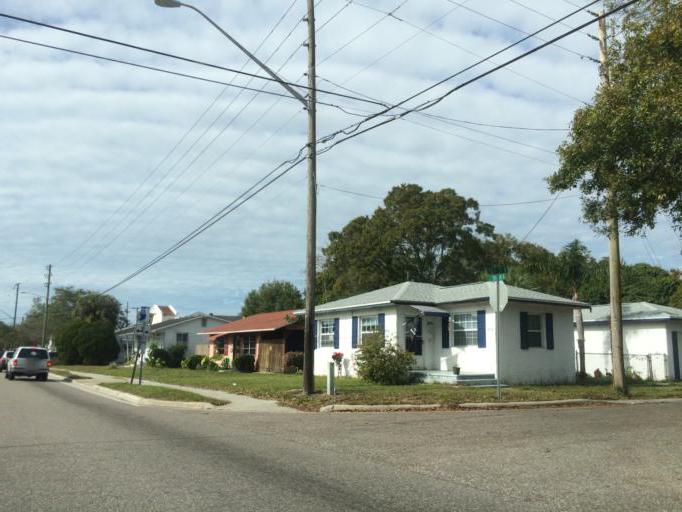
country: US
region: Florida
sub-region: Pinellas County
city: West and East Lealman
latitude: 27.8065
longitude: -82.6982
